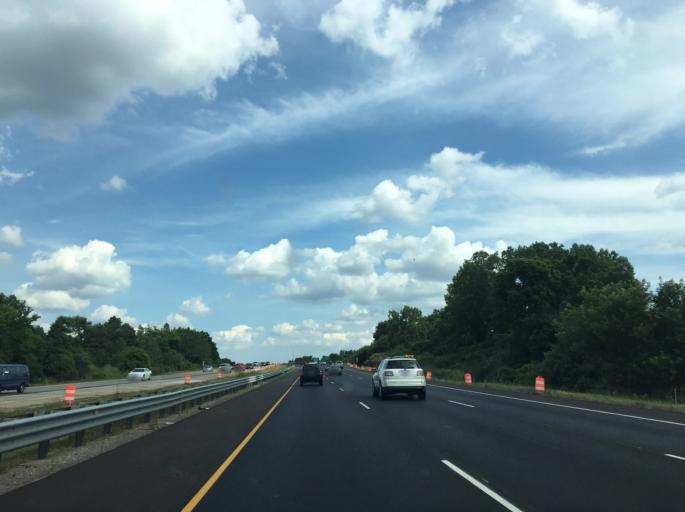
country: US
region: Michigan
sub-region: Oakland County
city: Waterford
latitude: 42.7123
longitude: -83.3374
